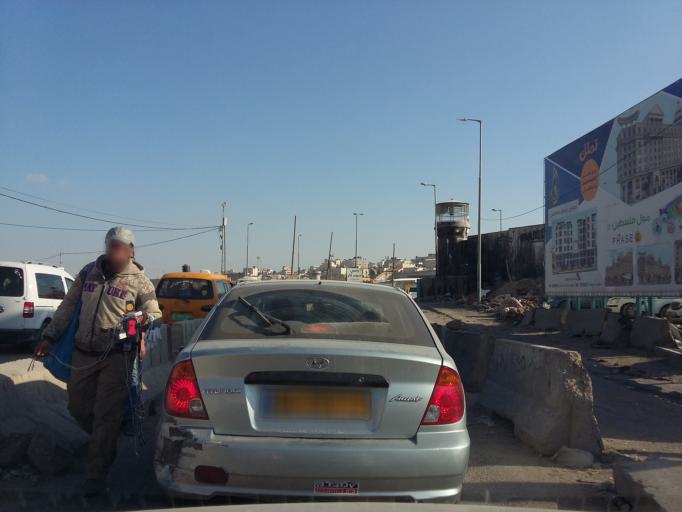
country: PS
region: West Bank
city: Ar Ram wa Dahiyat al Barid
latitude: 31.8639
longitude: 35.2275
